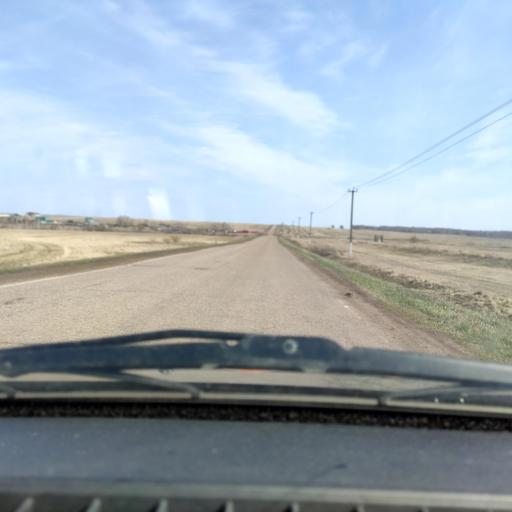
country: RU
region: Bashkortostan
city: Asanovo
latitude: 54.7788
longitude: 55.4993
